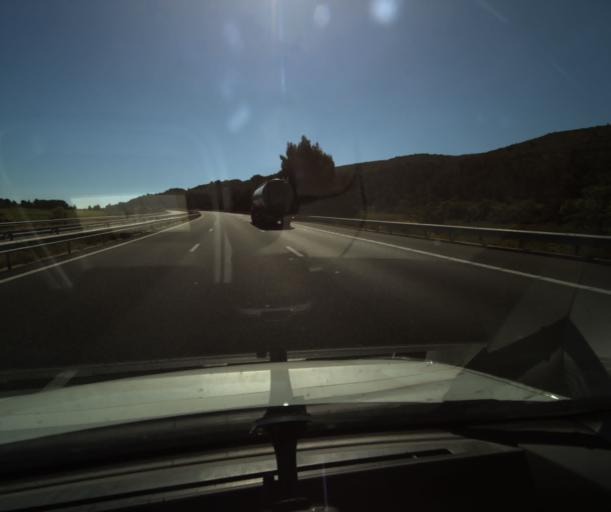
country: FR
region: Languedoc-Roussillon
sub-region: Departement de l'Aude
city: Puicheric
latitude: 43.1701
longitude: 2.6111
